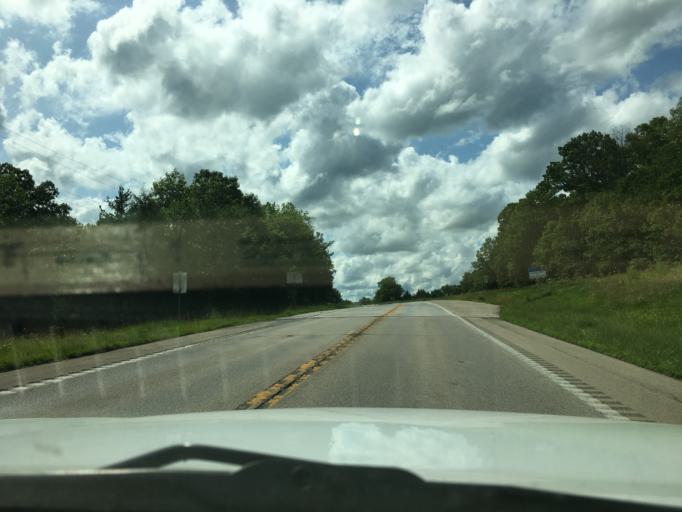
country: US
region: Missouri
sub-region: Franklin County
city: Gerald
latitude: 38.4222
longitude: -91.2593
